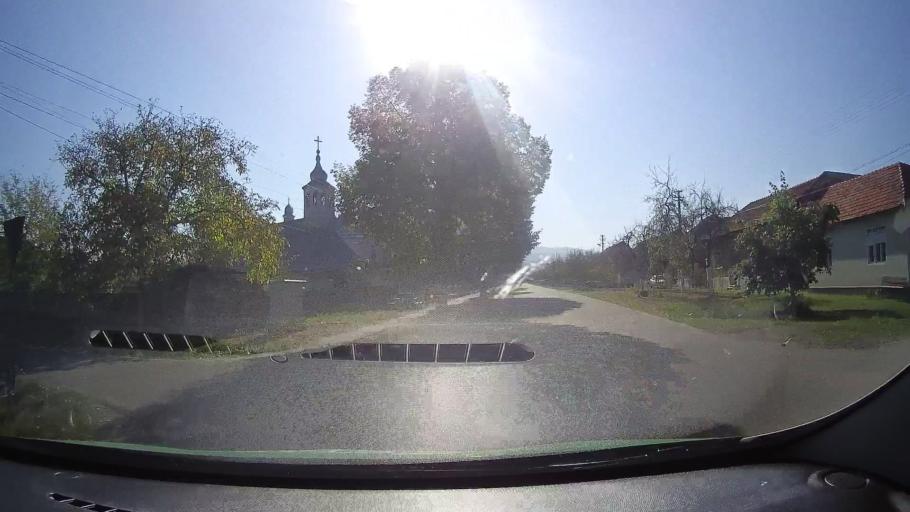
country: RO
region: Timis
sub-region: Comuna Curtea
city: Curtea
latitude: 45.8304
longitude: 22.3072
